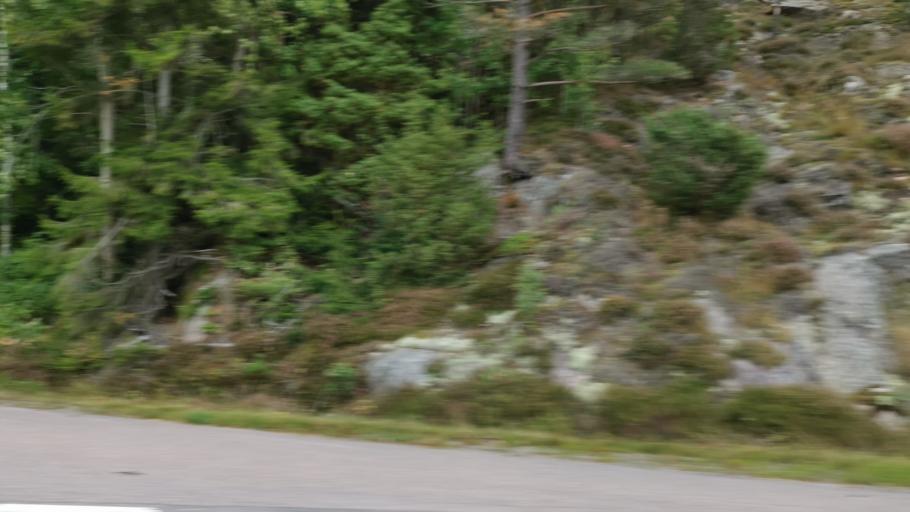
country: SE
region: Vaestra Goetaland
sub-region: Sotenas Kommun
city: Hunnebostrand
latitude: 58.5576
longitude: 11.4019
